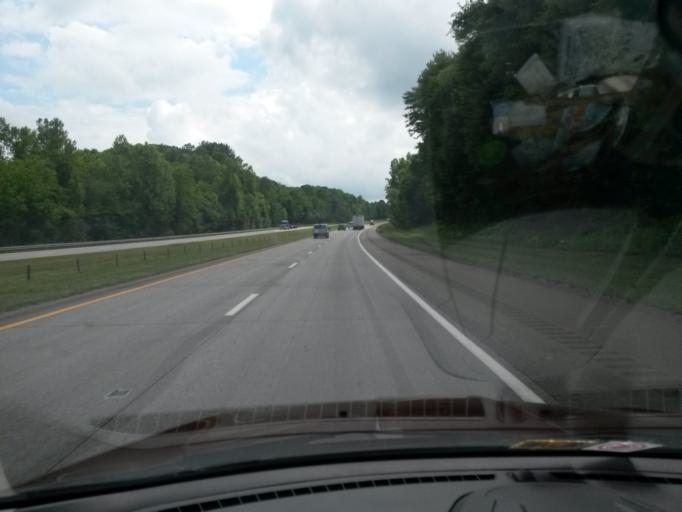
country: US
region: North Carolina
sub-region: Surry County
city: Elkin
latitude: 36.3083
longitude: -80.8052
